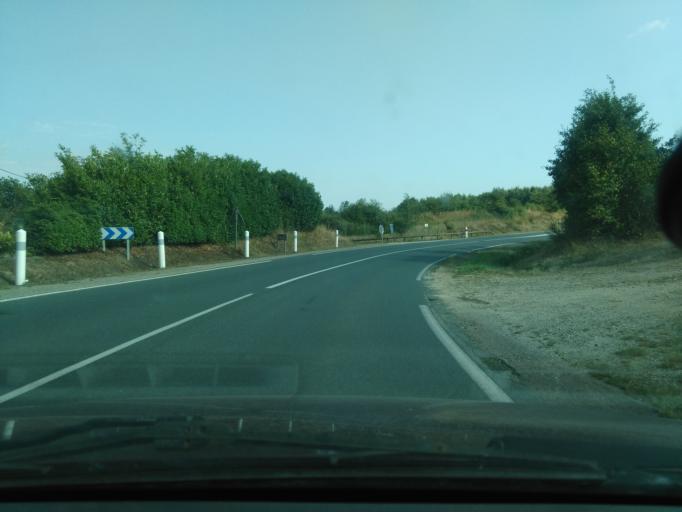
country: FR
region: Pays de la Loire
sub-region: Departement de la Vendee
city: La Roche-sur-Yon
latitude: 46.6400
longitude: -1.4407
